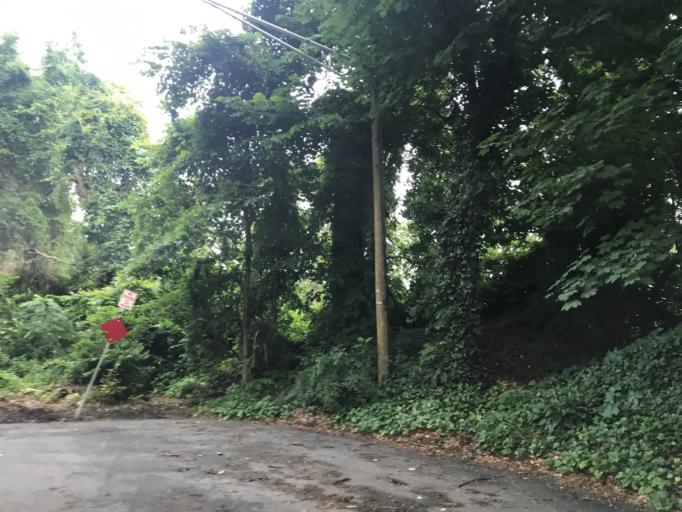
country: US
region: Maryland
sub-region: Baltimore County
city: Towson
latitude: 39.3737
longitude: -76.6046
